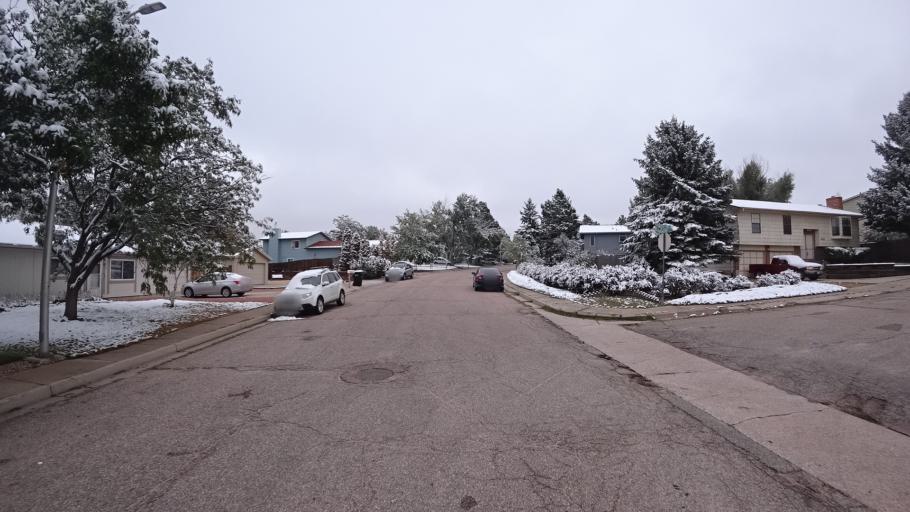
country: US
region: Colorado
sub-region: El Paso County
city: Cimarron Hills
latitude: 38.9234
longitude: -104.7727
